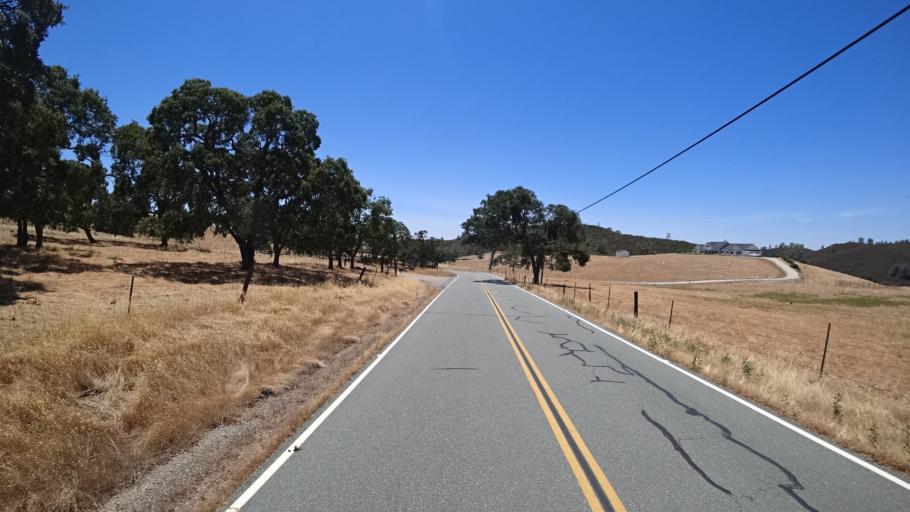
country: US
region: California
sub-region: Calaveras County
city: Valley Springs
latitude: 38.2378
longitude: -120.7932
